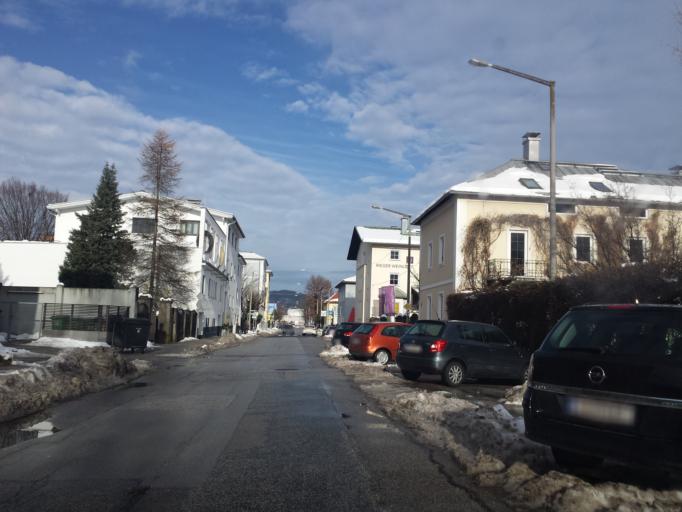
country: AT
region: Salzburg
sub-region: Salzburg Stadt
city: Salzburg
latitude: 47.8124
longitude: 13.0502
